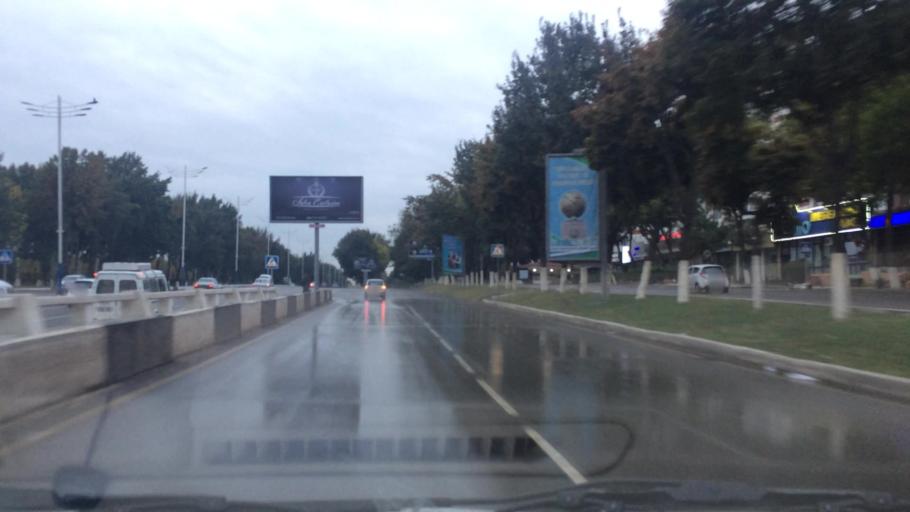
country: UZ
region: Toshkent Shahri
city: Tashkent
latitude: 41.3086
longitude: 69.2385
